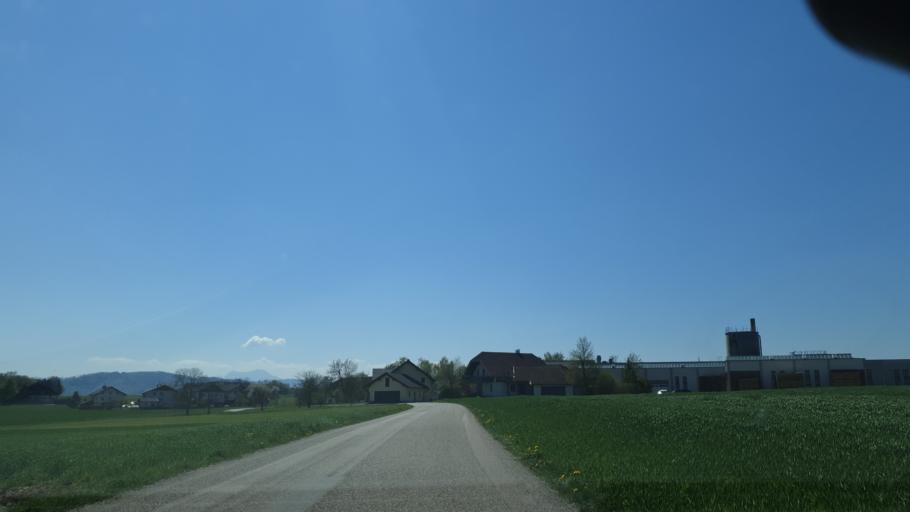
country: AT
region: Upper Austria
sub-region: Politischer Bezirk Vocklabruck
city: Gampern
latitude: 47.9807
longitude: 13.5467
